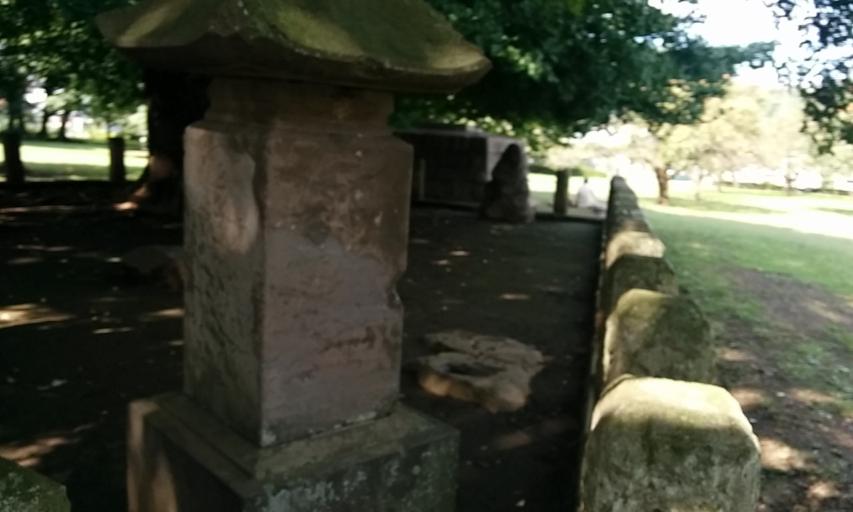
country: JP
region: Tokyo
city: Kokubunji
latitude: 35.6914
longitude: 139.4739
